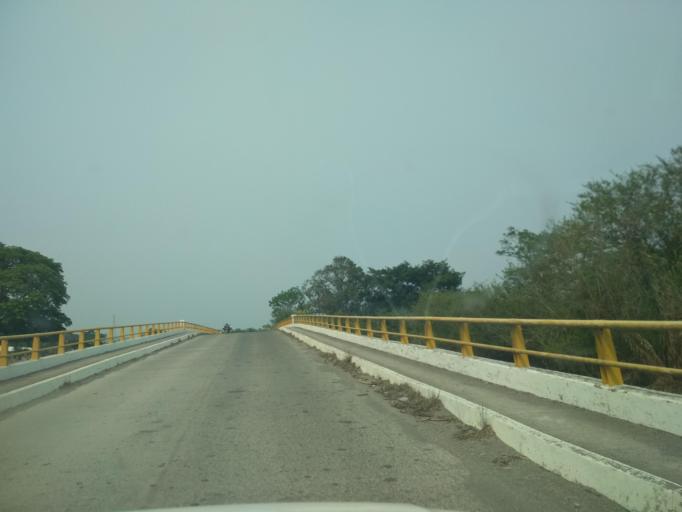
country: MX
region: Veracruz
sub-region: Veracruz
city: Delfino Victoria (Santa Fe)
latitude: 19.1907
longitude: -96.3059
